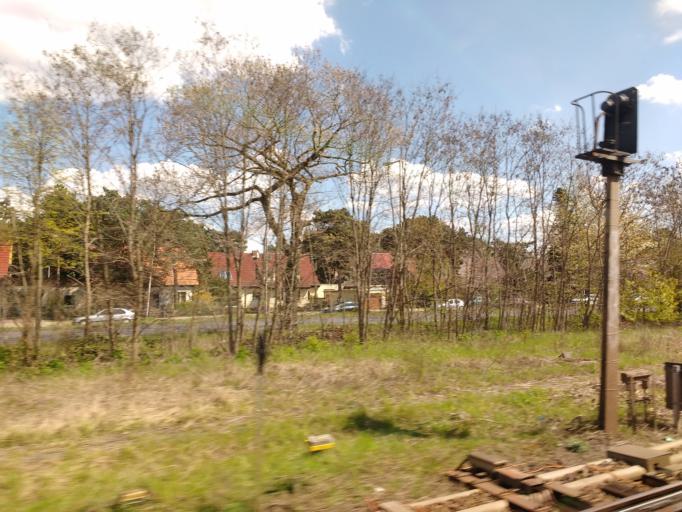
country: DE
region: Berlin
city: Adlershof
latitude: 52.4221
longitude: 13.5604
